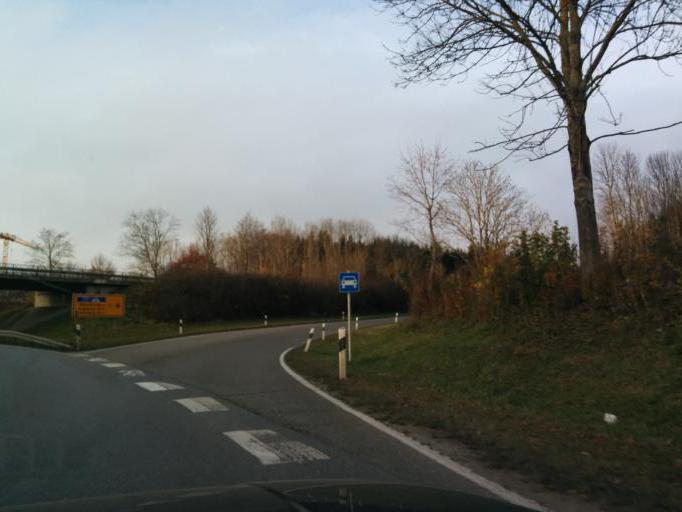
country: DE
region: Bavaria
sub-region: Swabia
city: Mauerstetten
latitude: 47.8974
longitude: 10.6492
